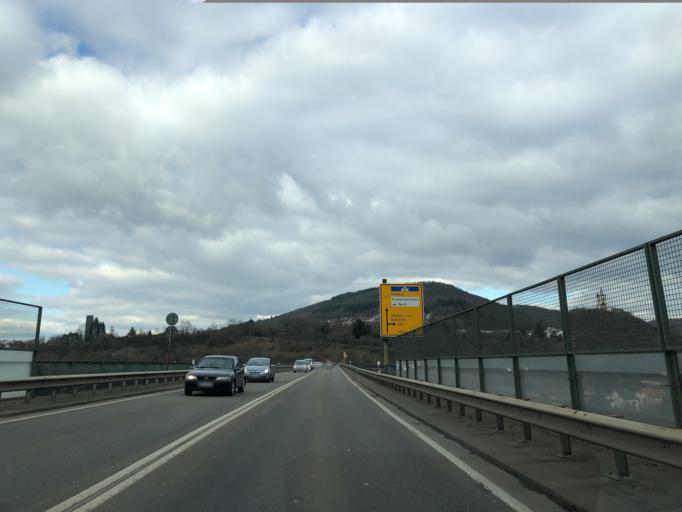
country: DE
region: Rheinland-Pfalz
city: Lahnstein
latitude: 50.3073
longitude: 7.6106
